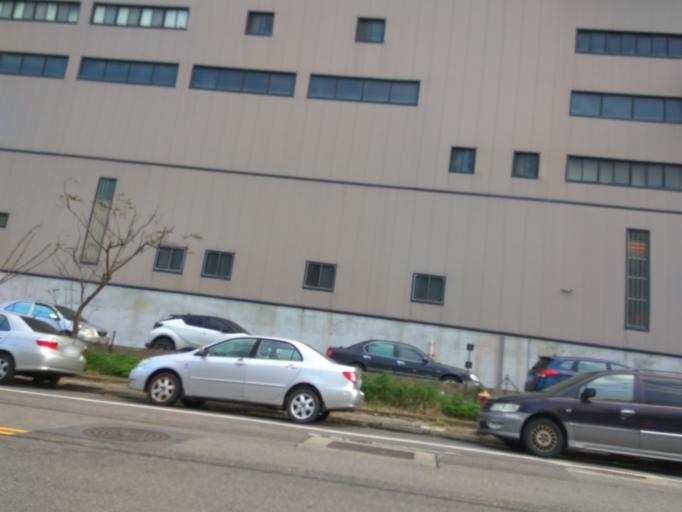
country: TW
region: Taiwan
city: Taoyuan City
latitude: 25.0610
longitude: 121.1765
